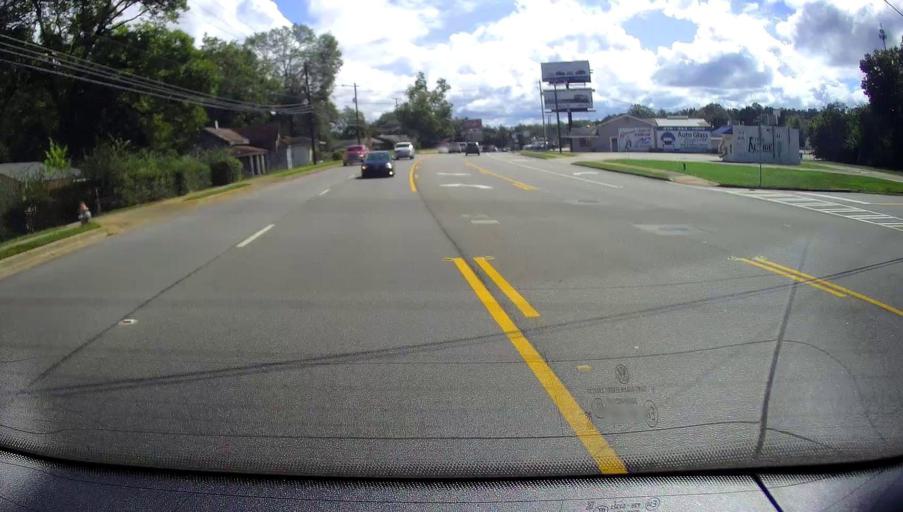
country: US
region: Georgia
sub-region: Baldwin County
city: Milledgeville
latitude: 33.0940
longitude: -83.2379
